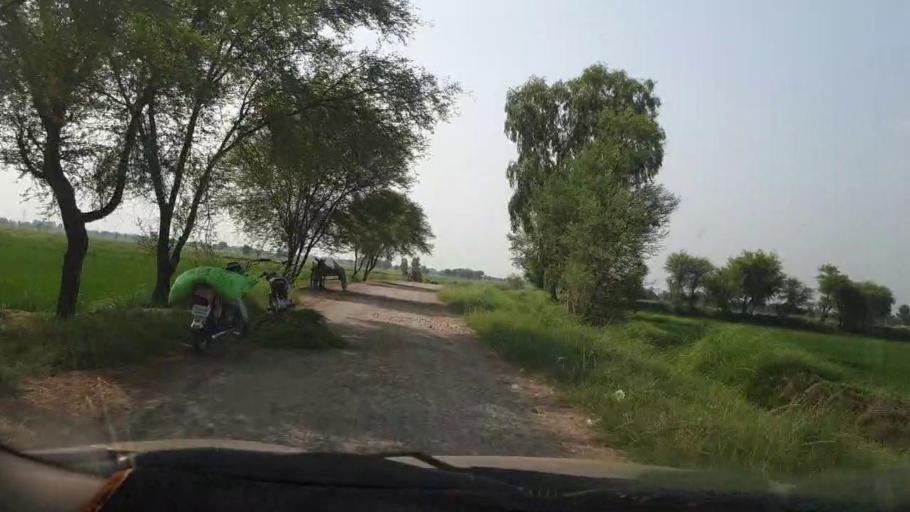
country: PK
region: Sindh
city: Goth Garelo
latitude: 27.4430
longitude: 68.0377
